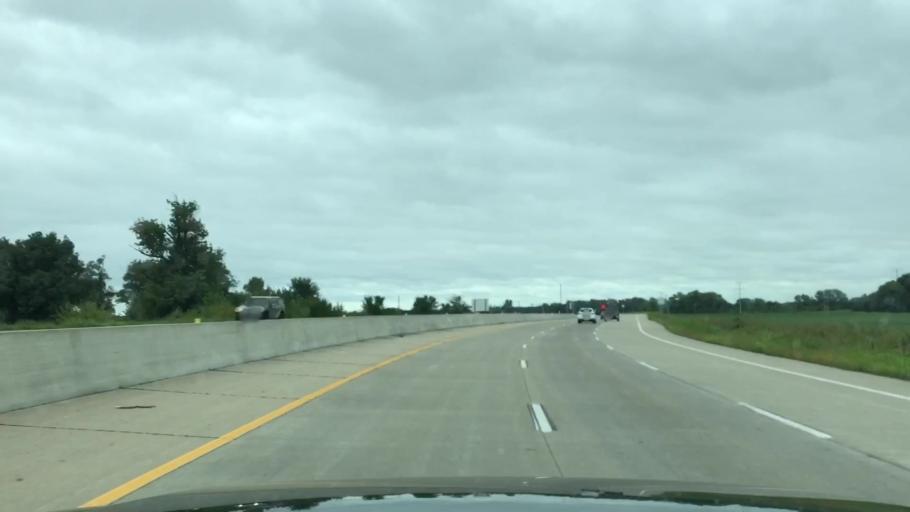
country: US
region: Missouri
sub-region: Saint Louis County
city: Maryland Heights
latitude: 38.7124
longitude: -90.5010
